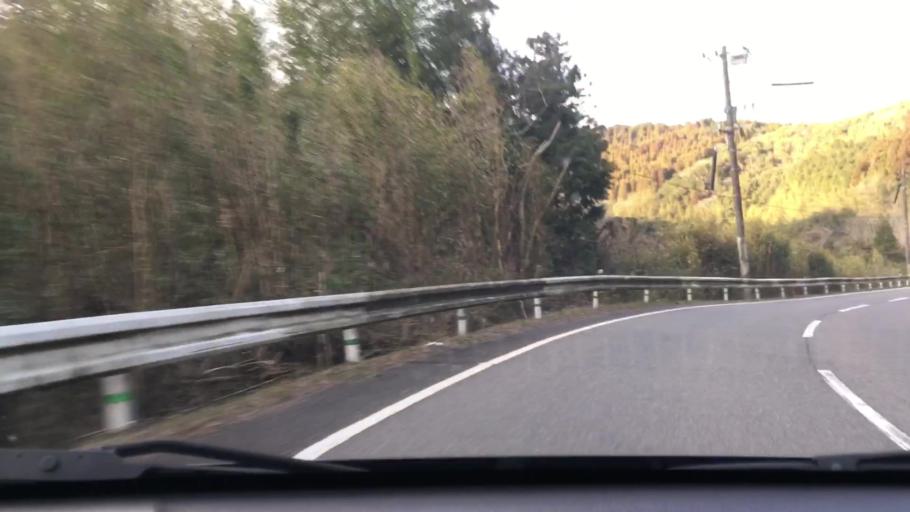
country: JP
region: Oita
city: Hiji
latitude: 33.4168
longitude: 131.4189
